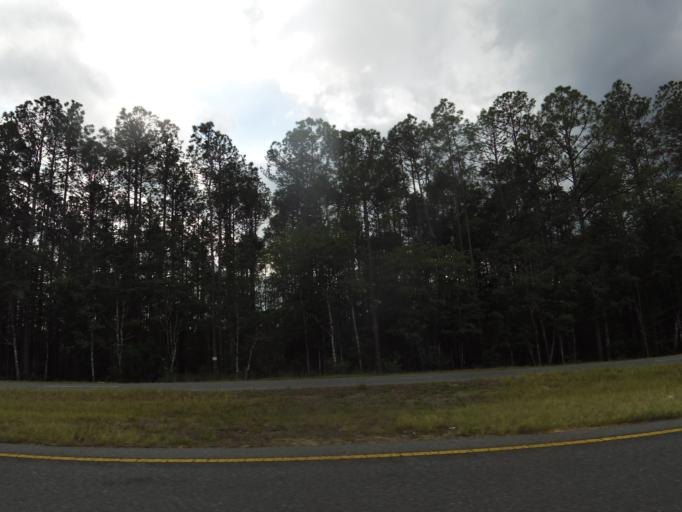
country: US
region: Georgia
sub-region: Charlton County
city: Folkston
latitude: 30.8515
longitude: -81.9332
